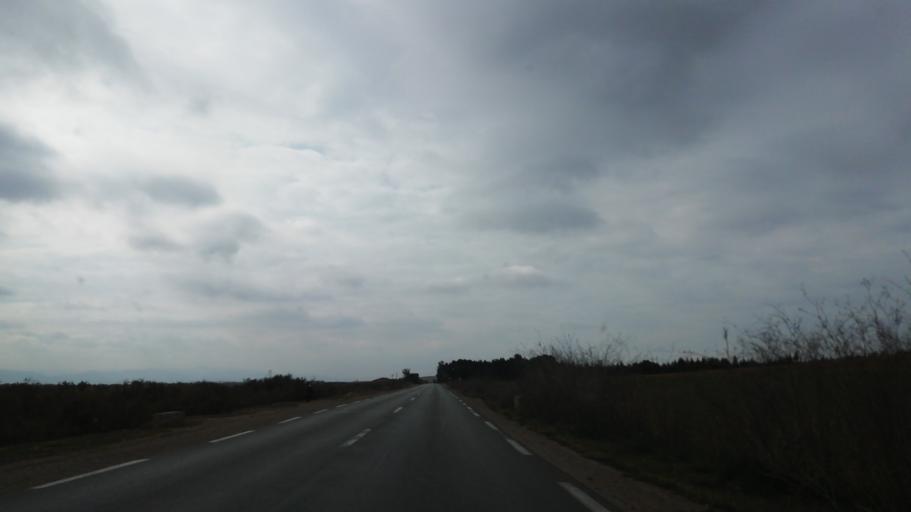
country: DZ
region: Oran
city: Sidi ech Chahmi
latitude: 35.6040
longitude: -0.4366
